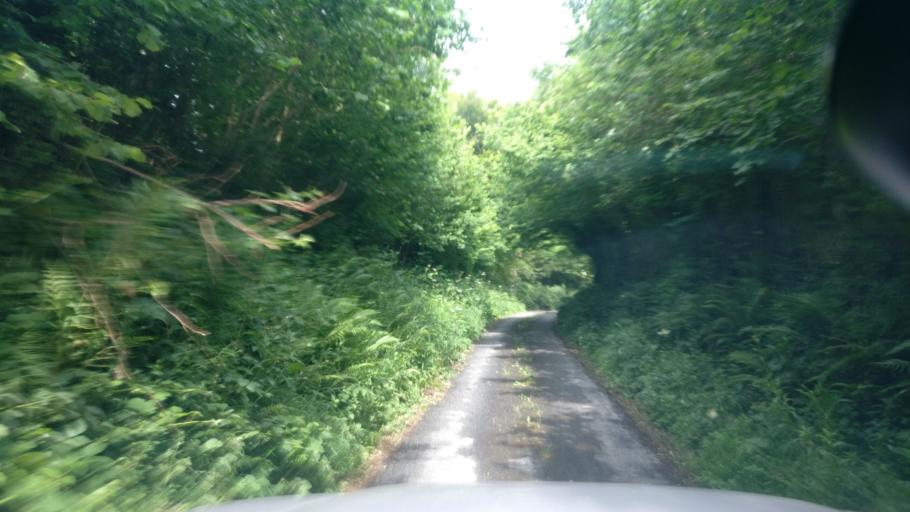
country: IE
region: Connaught
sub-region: County Galway
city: Ballinasloe
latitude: 53.2794
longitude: -8.3239
